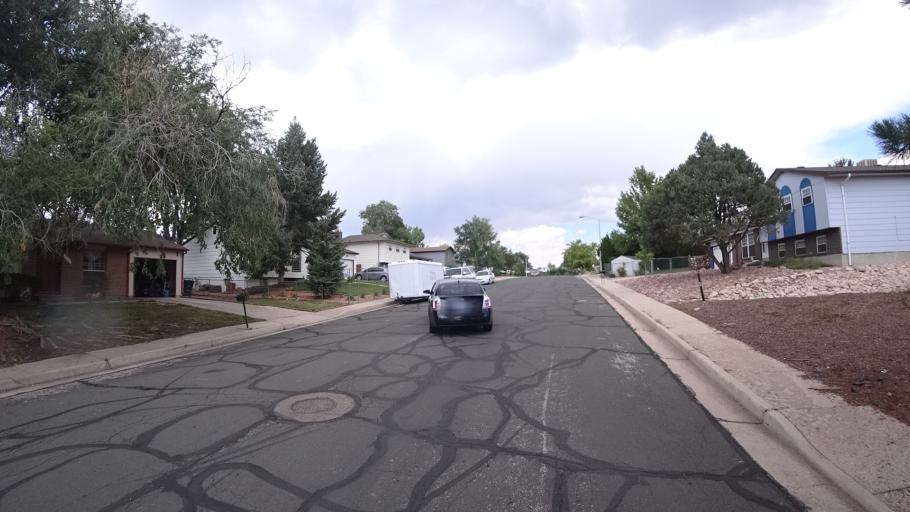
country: US
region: Colorado
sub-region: El Paso County
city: Cimarron Hills
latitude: 38.8314
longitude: -104.7414
